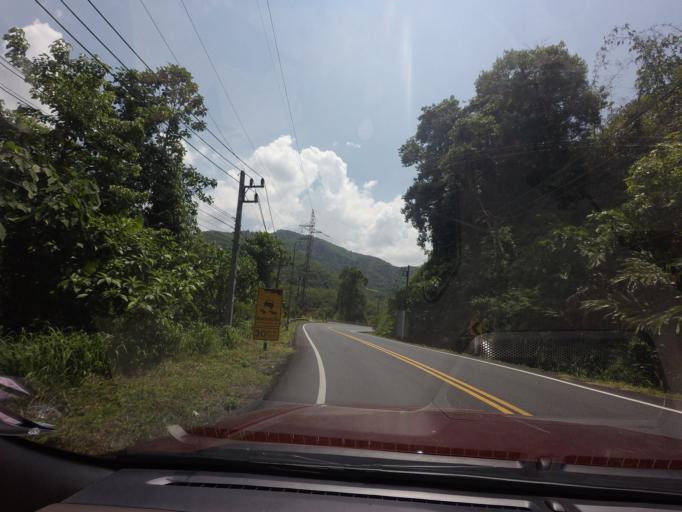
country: TH
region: Yala
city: Betong
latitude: 5.9048
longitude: 101.1485
